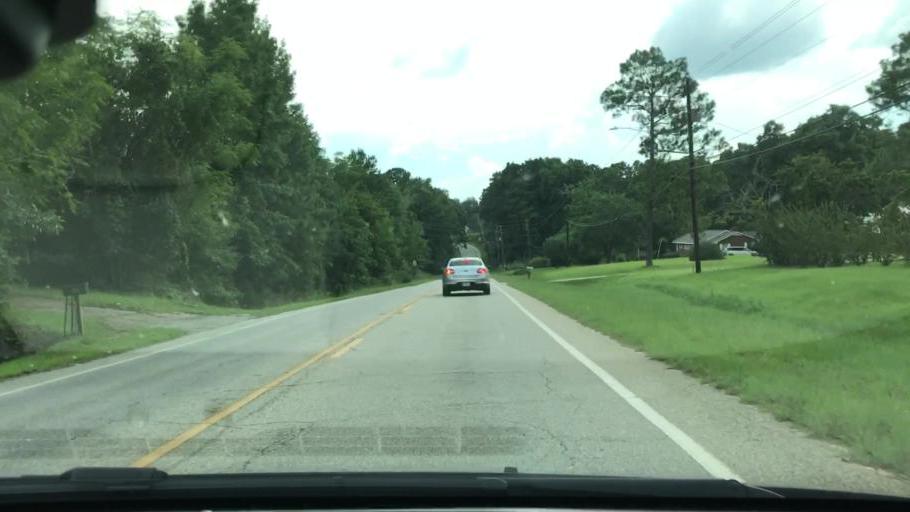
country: US
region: Georgia
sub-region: Clay County
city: Fort Gaines
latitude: 31.6167
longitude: -85.0467
